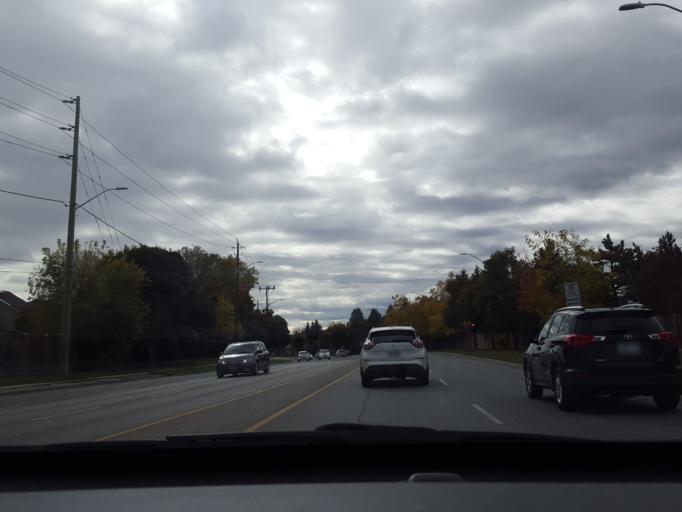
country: CA
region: Ontario
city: Markham
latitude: 43.8790
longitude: -79.3142
